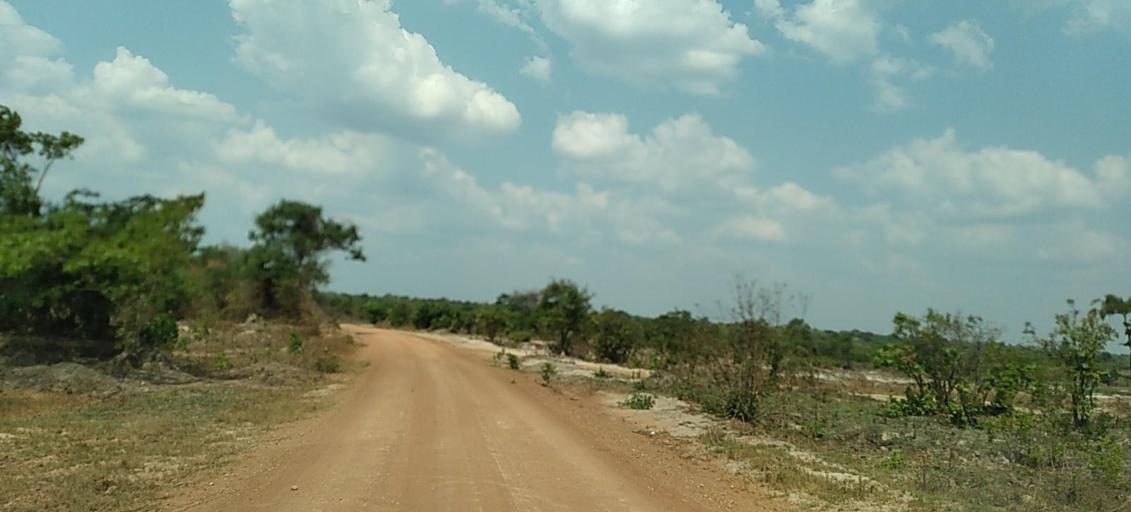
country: ZM
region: Copperbelt
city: Luanshya
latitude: -13.1379
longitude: 28.3411
